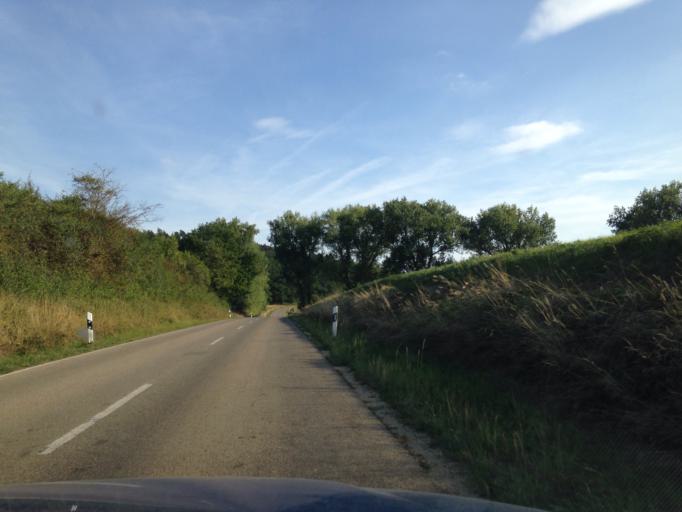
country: DE
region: Bavaria
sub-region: Regierungsbezirk Mittelfranken
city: Thalmassing
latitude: 49.1252
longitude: 11.2117
